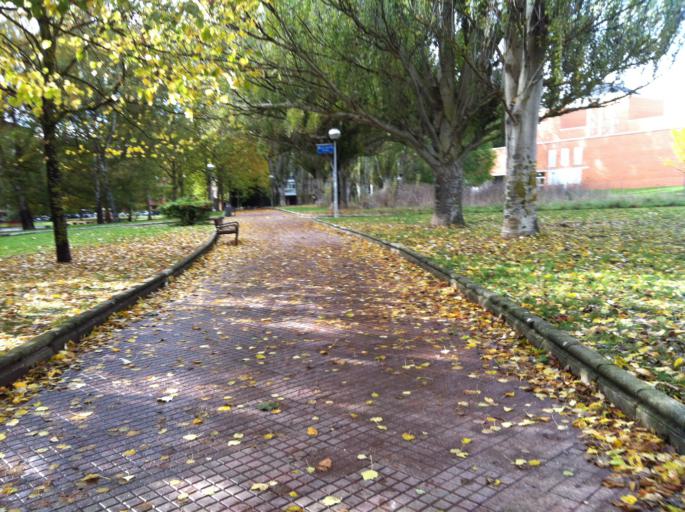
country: ES
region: Basque Country
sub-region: Provincia de Alava
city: Gasteiz / Vitoria
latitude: 42.8543
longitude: -2.6952
